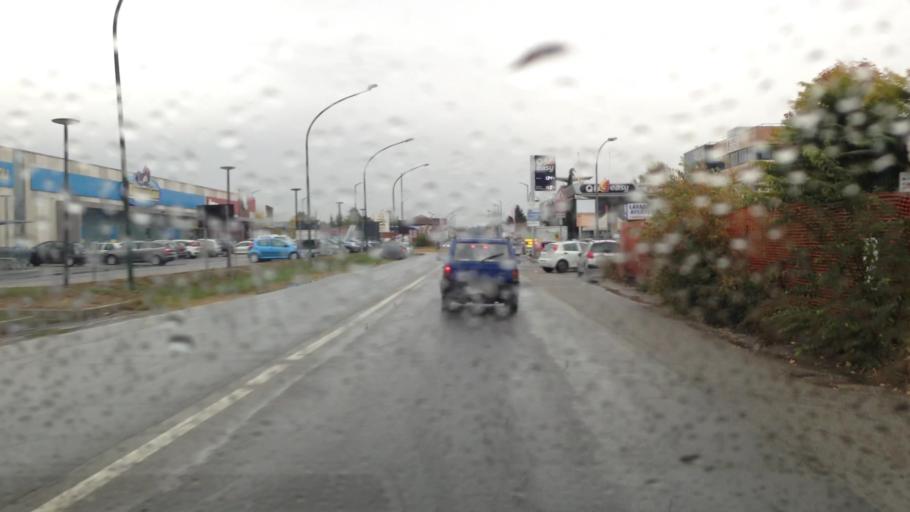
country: IT
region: Piedmont
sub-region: Provincia di Asti
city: Asti
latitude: 44.9058
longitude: 8.2326
